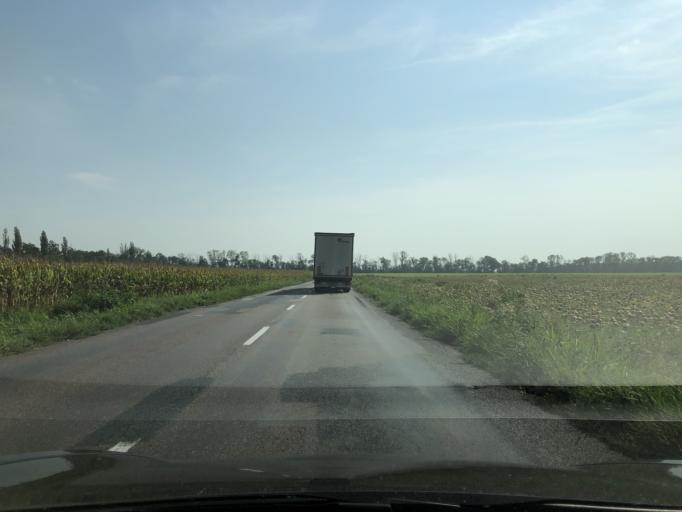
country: CZ
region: South Moravian
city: Brezi
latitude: 48.8254
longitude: 16.5403
